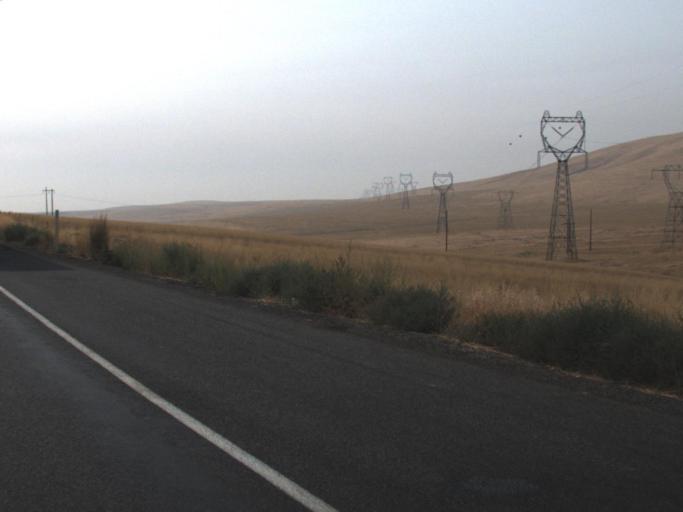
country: US
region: Washington
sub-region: Yakima County
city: Sunnyside
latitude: 46.4705
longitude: -119.9326
